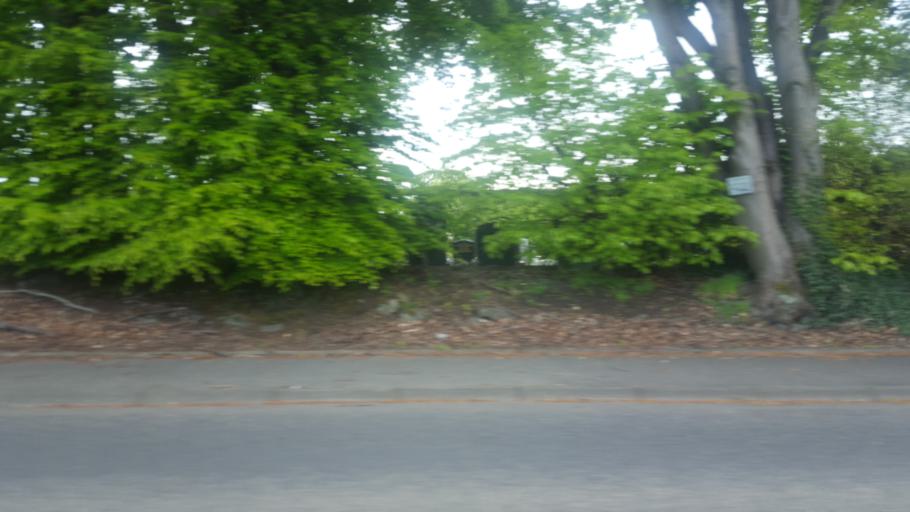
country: GB
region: Scotland
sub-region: Falkirk
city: Polmont
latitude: 55.9956
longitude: -3.7072
